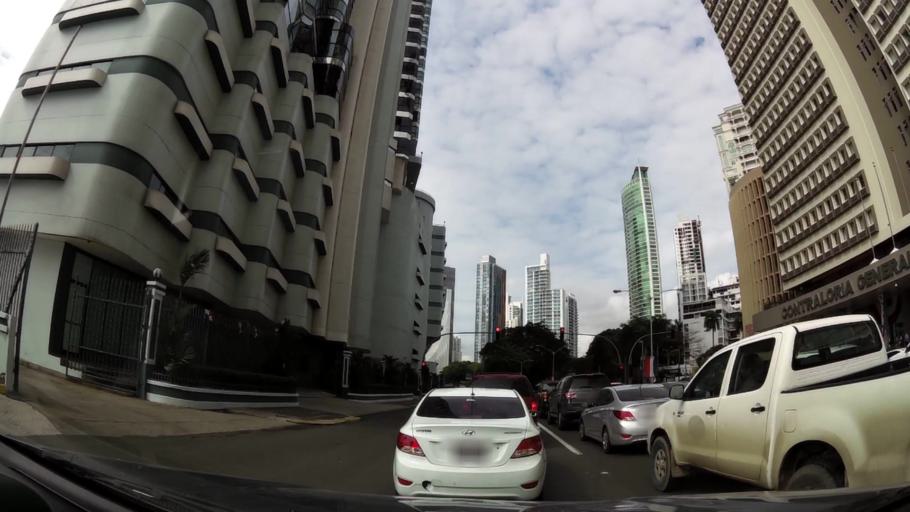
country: PA
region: Panama
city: Panama
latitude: 8.9754
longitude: -79.5258
